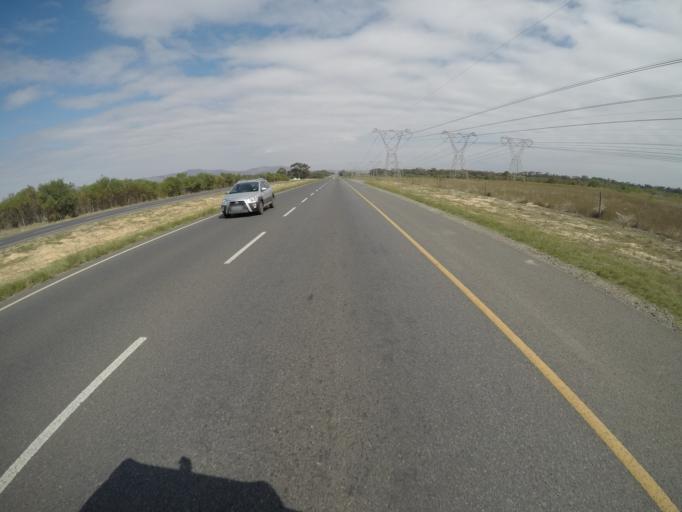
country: ZA
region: Western Cape
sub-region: City of Cape Town
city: Sunset Beach
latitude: -33.7393
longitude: 18.5454
